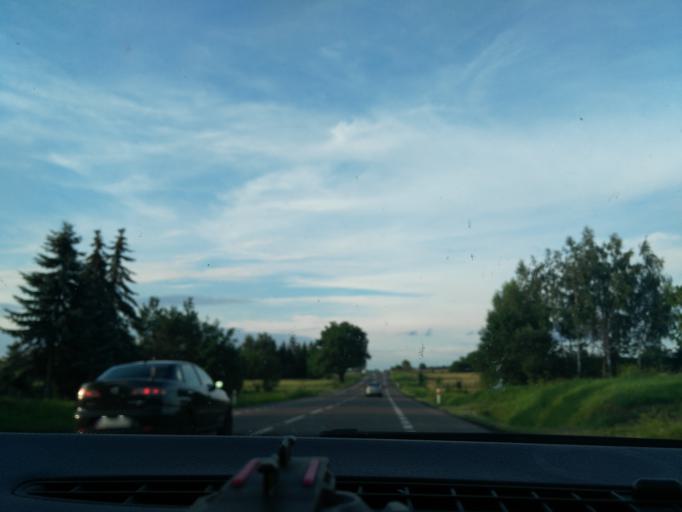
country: PL
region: Lublin Voivodeship
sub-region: Powiat krasnicki
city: Wilkolaz
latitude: 51.0154
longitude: 22.3519
